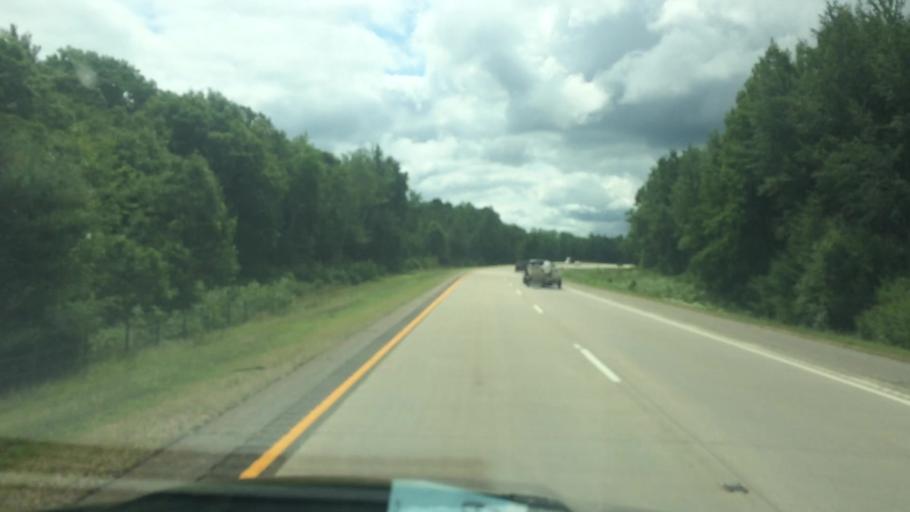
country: US
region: Wisconsin
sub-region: Marathon County
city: Mosinee
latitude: 44.6918
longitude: -89.6435
